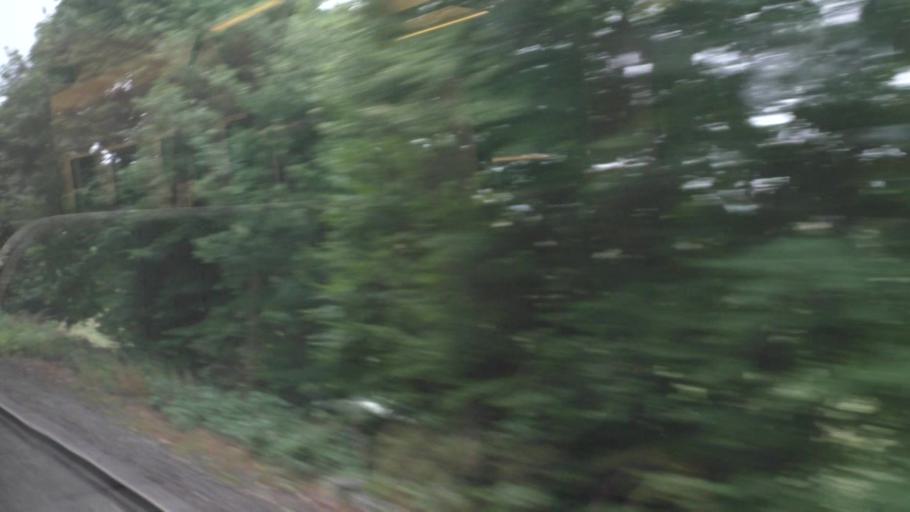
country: DE
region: Saxony
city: Bischofswerda
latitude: 51.1148
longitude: 14.1599
